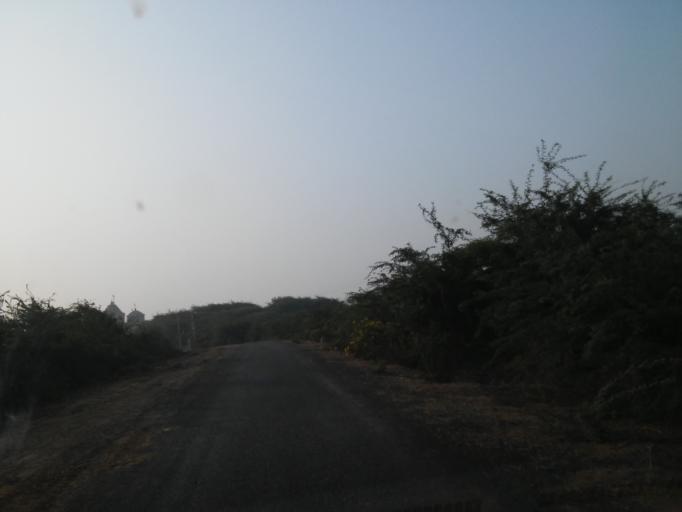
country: IN
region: Gujarat
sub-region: Kachchh
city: Mandvi
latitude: 22.8168
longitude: 69.3900
